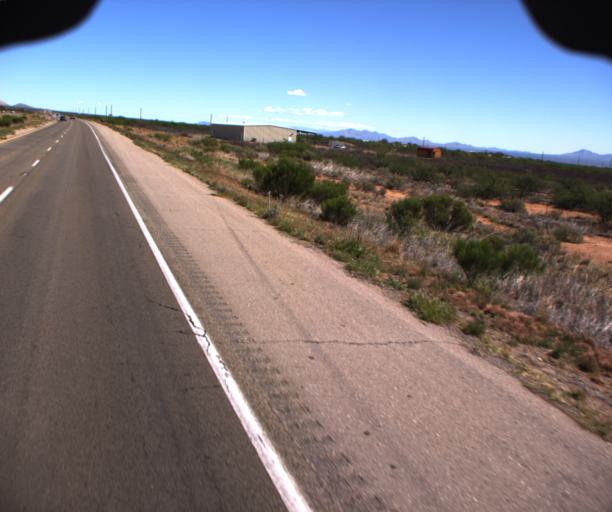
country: US
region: Arizona
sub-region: Cochise County
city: Huachuca City
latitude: 31.7238
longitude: -110.3501
